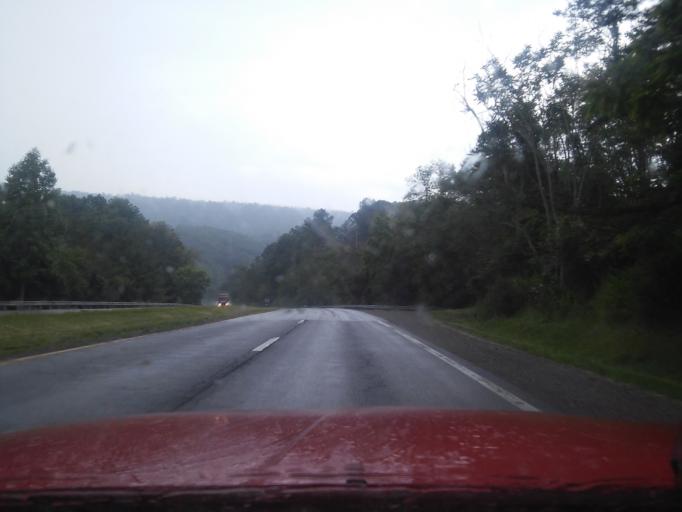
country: US
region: Virginia
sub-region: Montgomery County
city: Prices Fork
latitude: 37.2948
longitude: -80.5017
